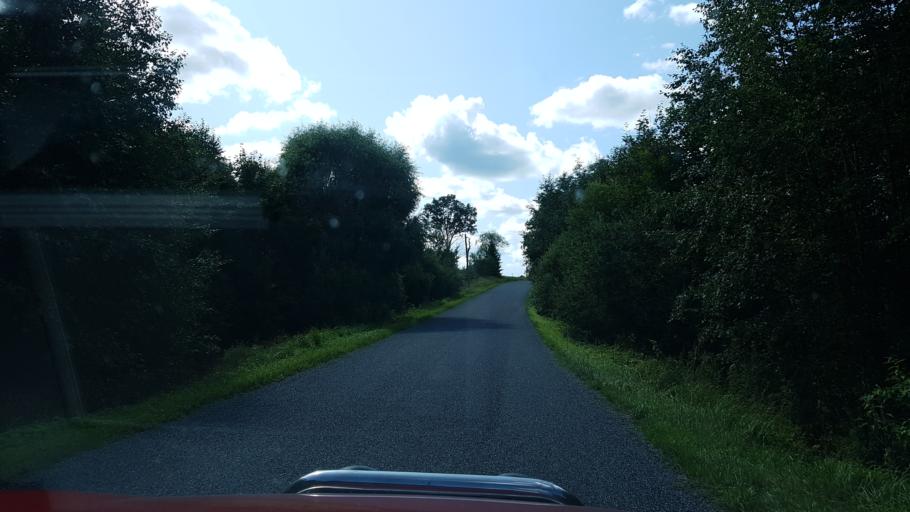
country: EE
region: Vorumaa
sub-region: Voru linn
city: Voru
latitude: 57.7283
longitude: 27.2681
